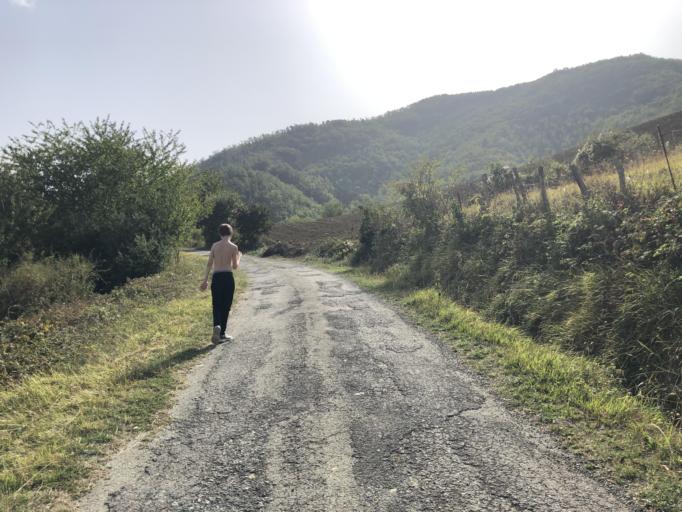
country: IT
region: Emilia-Romagna
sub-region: Forli-Cesena
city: Portico e San Benedetto
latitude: 44.0208
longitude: 11.7876
